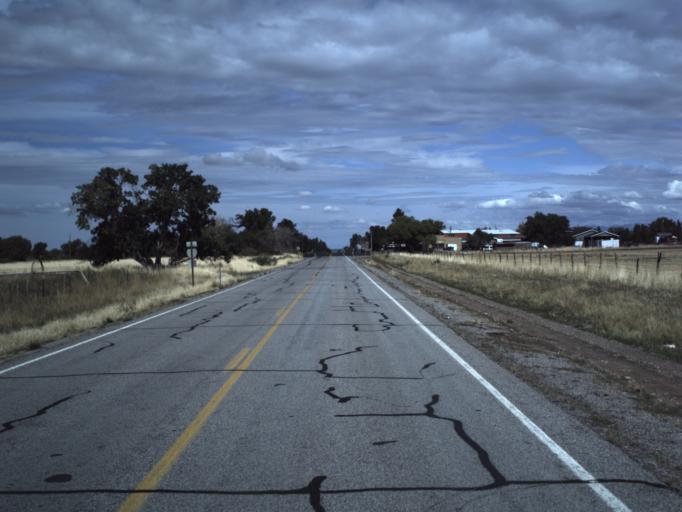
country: US
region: Utah
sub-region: Millard County
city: Fillmore
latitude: 38.7920
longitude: -112.4376
